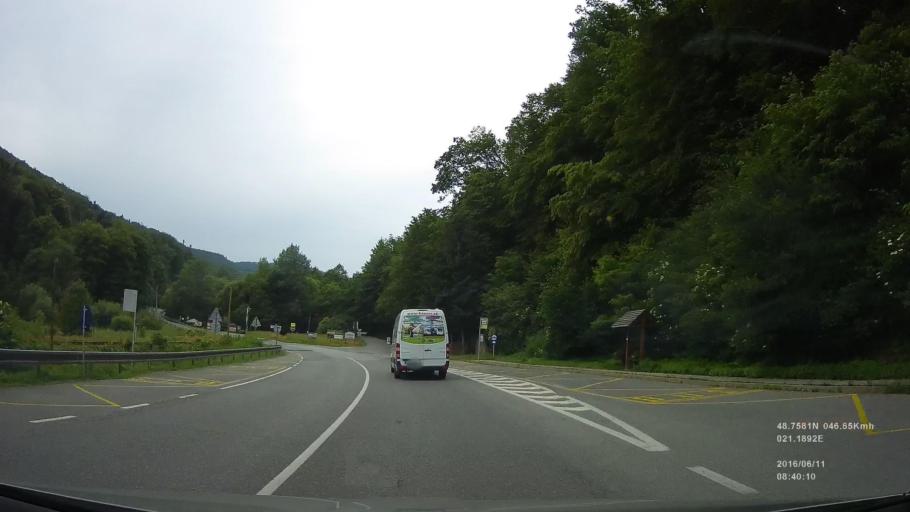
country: SK
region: Kosicky
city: Kosice
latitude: 48.7476
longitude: 21.2358
